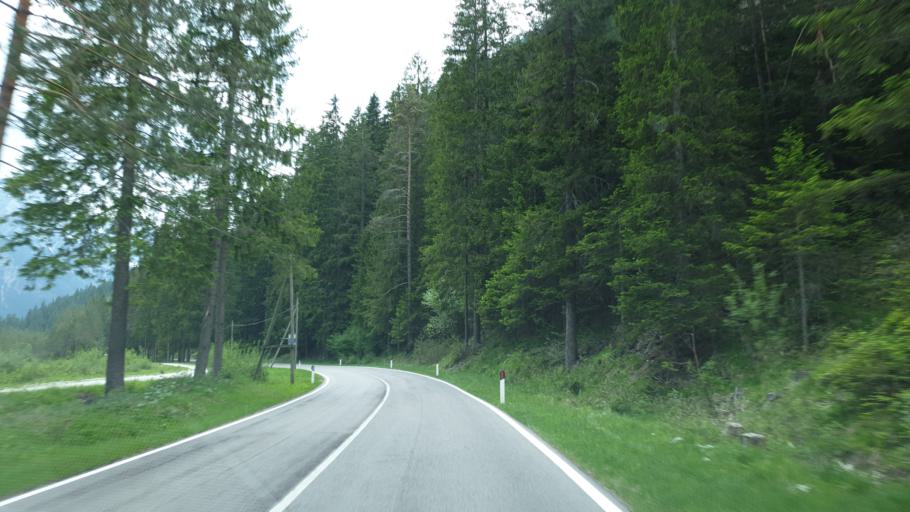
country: IT
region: Veneto
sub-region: Provincia di Belluno
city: Auronzo
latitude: 46.5650
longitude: 12.3477
